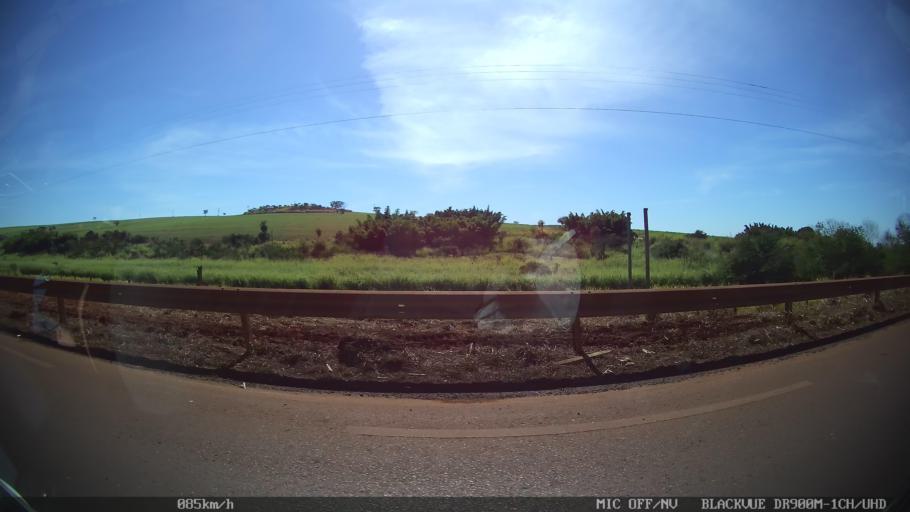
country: BR
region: Sao Paulo
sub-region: Ipua
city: Ipua
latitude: -20.4925
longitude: -48.0070
